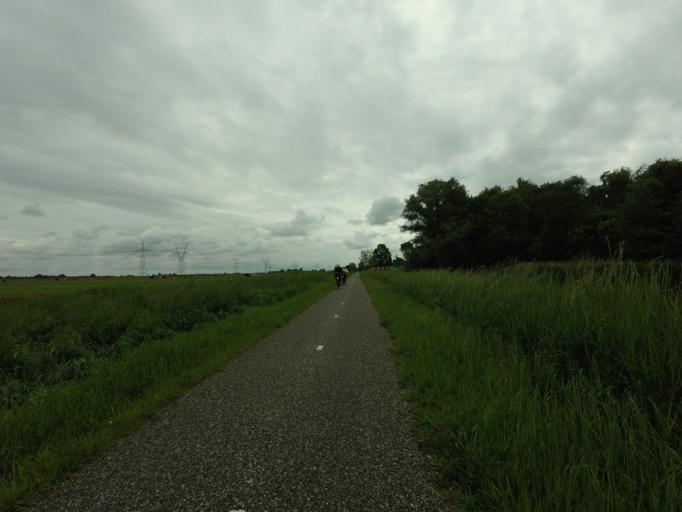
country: NL
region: North Holland
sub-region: Gemeente Waterland
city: Broek in Waterland
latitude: 52.3929
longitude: 4.9700
